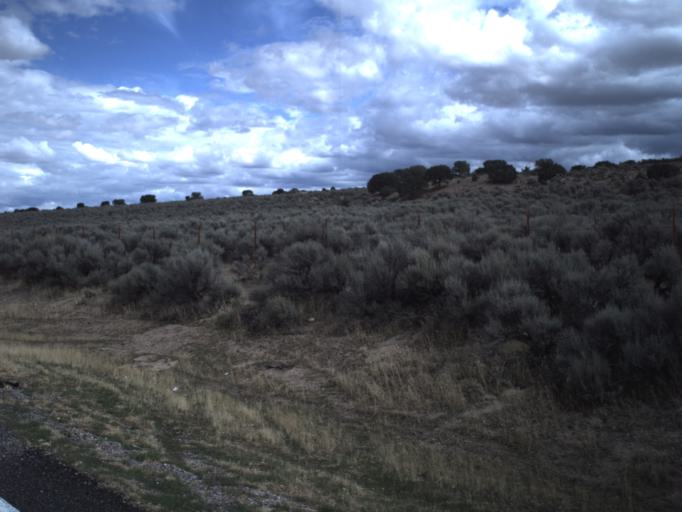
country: US
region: Utah
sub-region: Millard County
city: Fillmore
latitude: 39.0054
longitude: -112.4111
